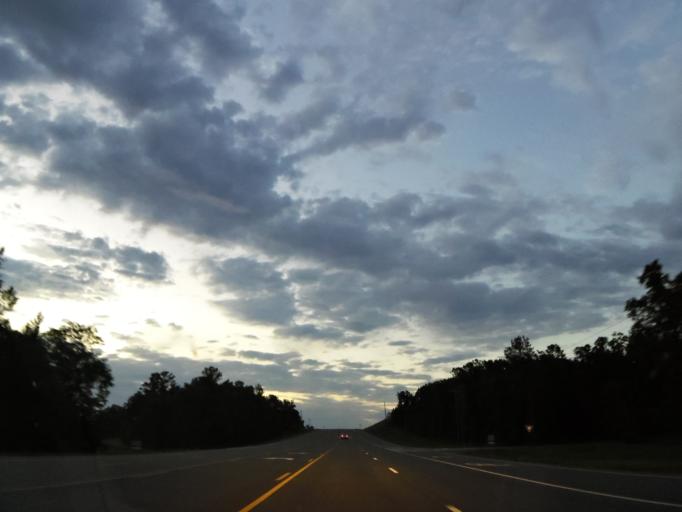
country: US
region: Alabama
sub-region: Marion County
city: Winfield
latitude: 33.9795
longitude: -87.7751
